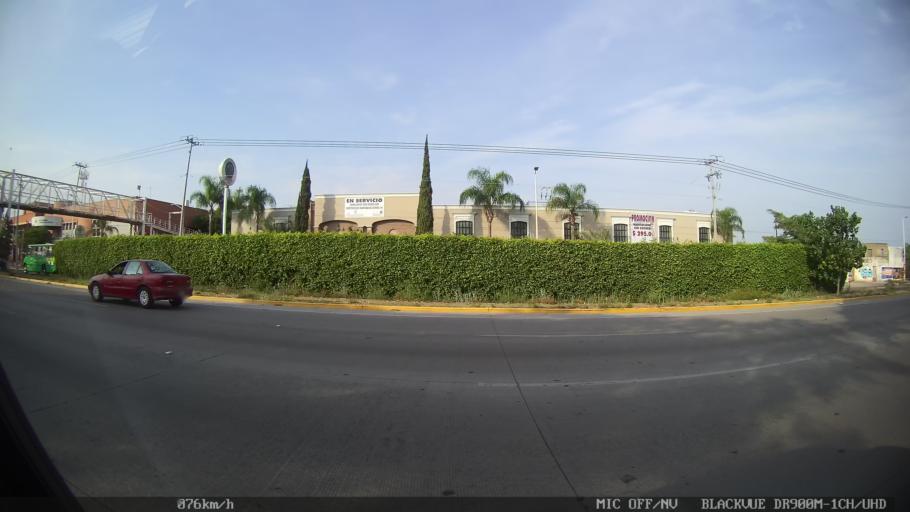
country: MX
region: Jalisco
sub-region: Zapopan
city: Zapopan
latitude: 20.7184
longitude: -103.3128
